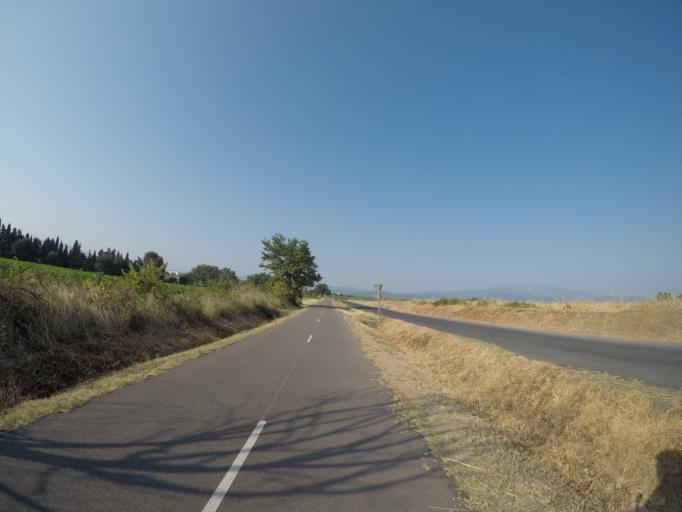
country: FR
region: Languedoc-Roussillon
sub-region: Departement des Pyrenees-Orientales
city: Ponteilla
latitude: 42.6339
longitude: 2.8077
